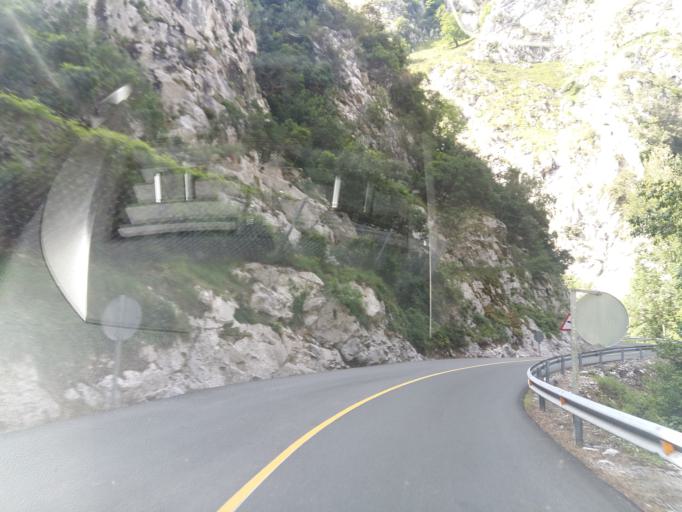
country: ES
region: Cantabria
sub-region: Provincia de Cantabria
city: Tresviso
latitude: 43.2414
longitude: -4.5822
